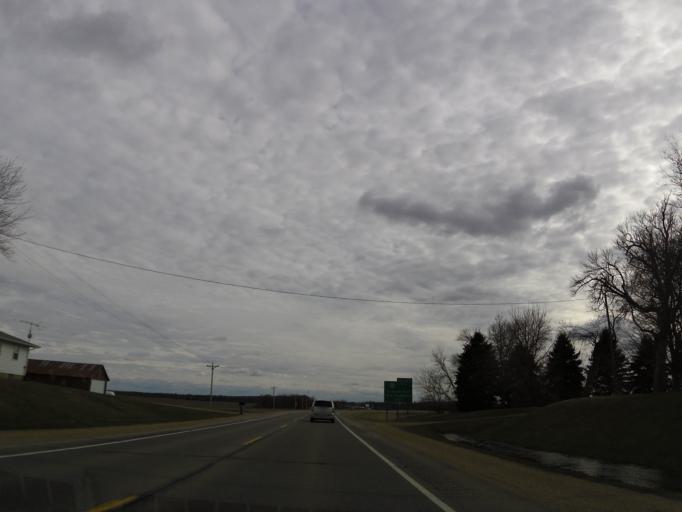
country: US
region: Iowa
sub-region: Chickasaw County
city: New Hampton
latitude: 43.0954
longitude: -92.2981
